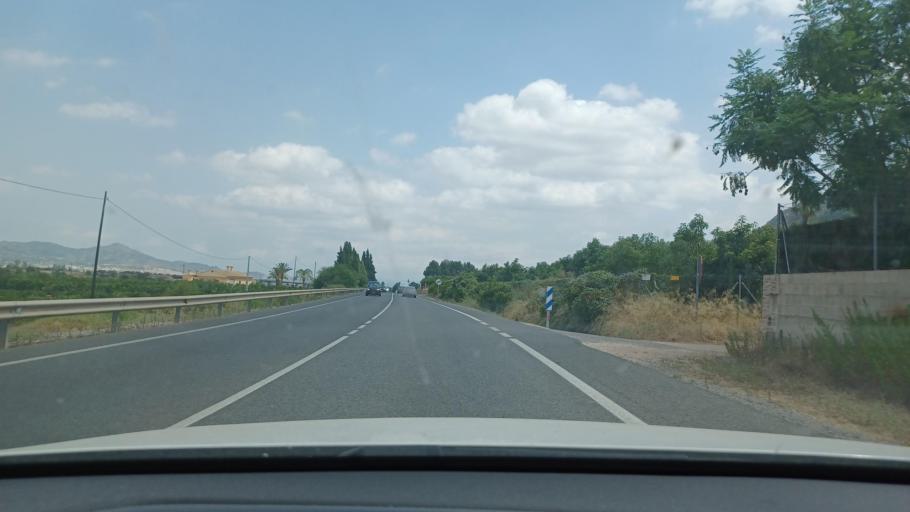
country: ES
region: Valencia
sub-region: Provincia de Valencia
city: Valles
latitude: 38.9727
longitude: -0.5588
